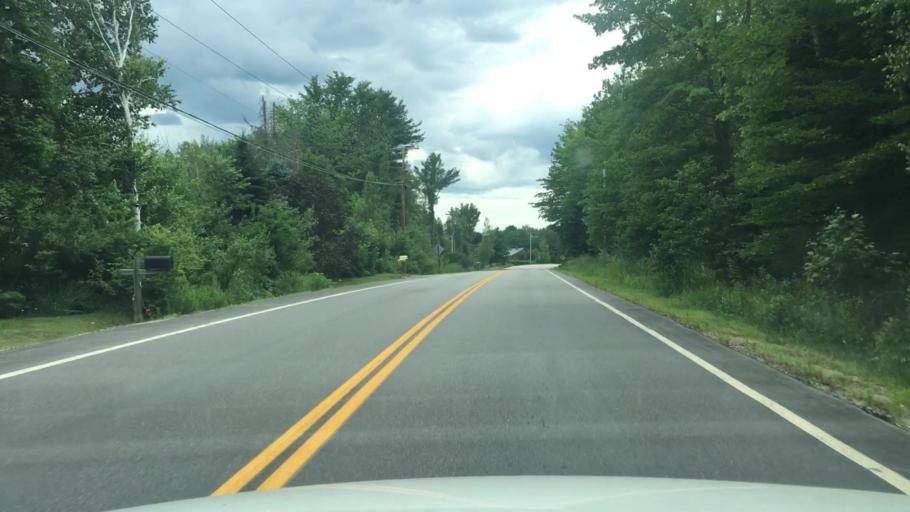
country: US
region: Maine
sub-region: Oxford County
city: West Paris
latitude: 44.3419
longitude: -70.5306
